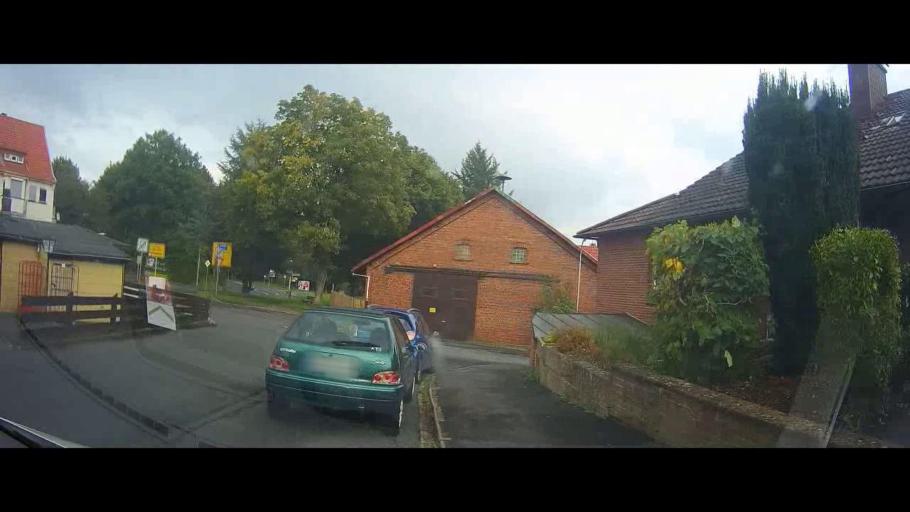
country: DE
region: Lower Saxony
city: Uslar
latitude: 51.6396
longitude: 9.6567
